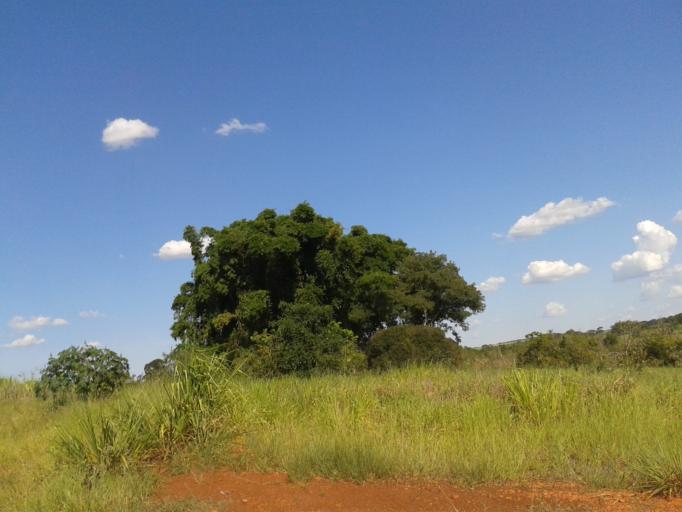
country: BR
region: Minas Gerais
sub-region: Santa Vitoria
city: Santa Vitoria
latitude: -19.1307
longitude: -50.4847
